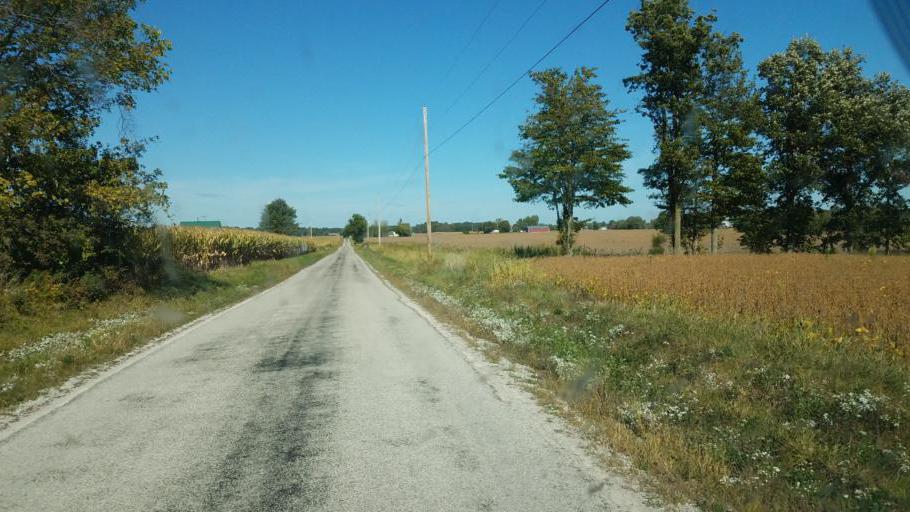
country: US
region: Ohio
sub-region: Huron County
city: Willard
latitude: 40.9525
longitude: -82.7972
